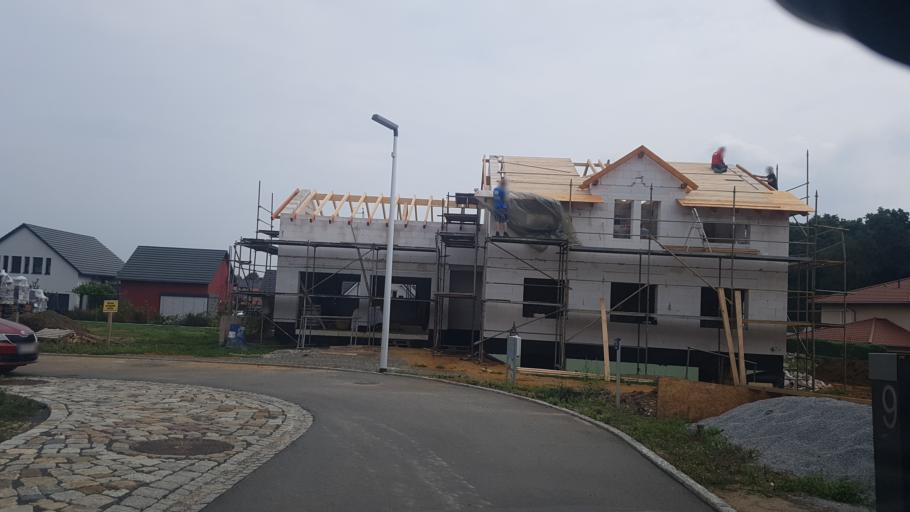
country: DE
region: Saxony
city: Horka
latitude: 51.2807
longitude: 14.2337
